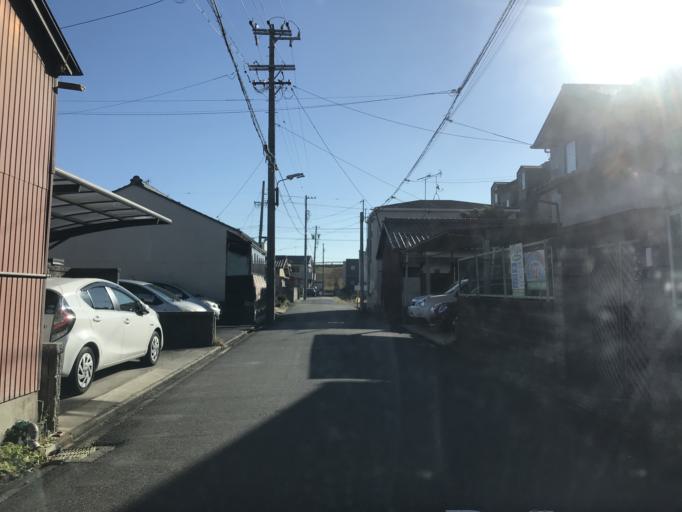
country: JP
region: Aichi
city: Nagoya-shi
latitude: 35.2022
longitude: 136.8725
